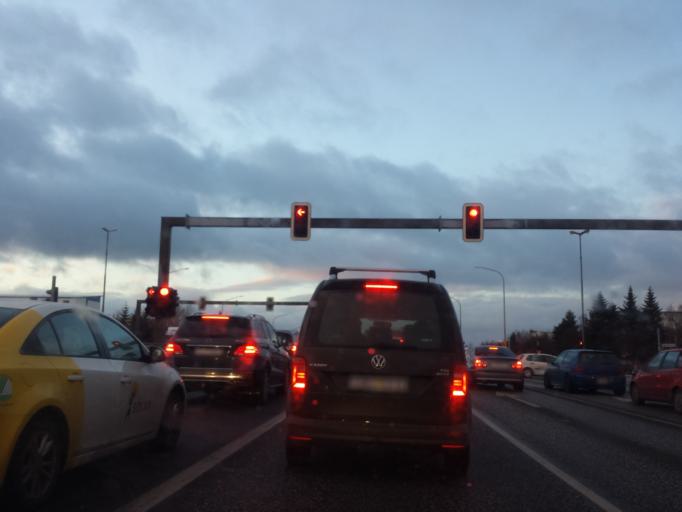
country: IS
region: Capital Region
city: Reykjavik
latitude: 64.1309
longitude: -21.8829
